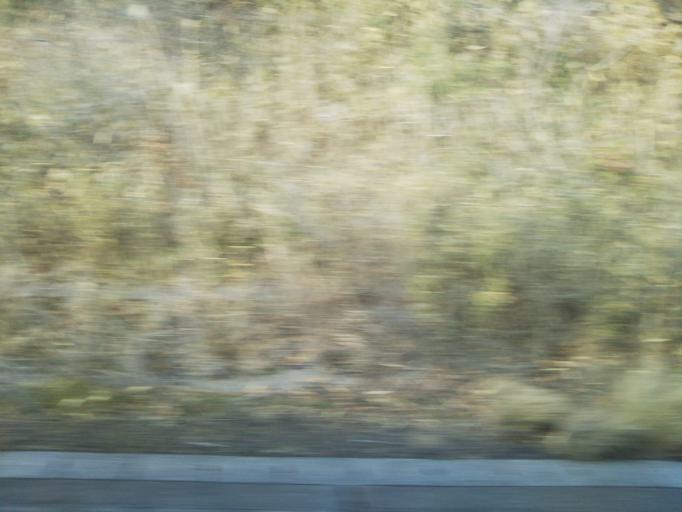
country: JP
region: Kagawa
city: Sakaidecho
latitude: 34.4539
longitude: 133.8071
